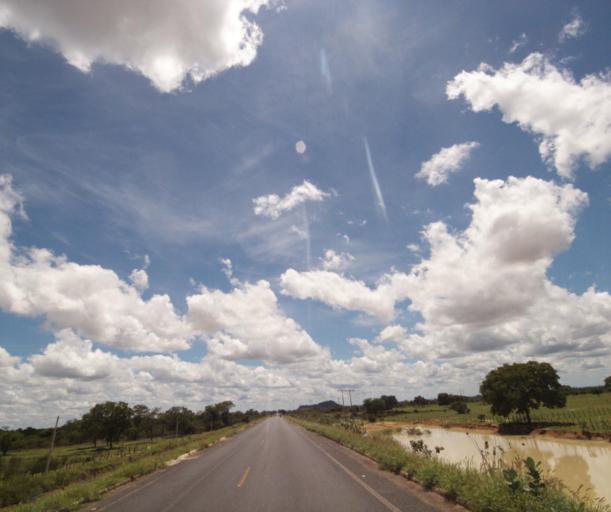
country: BR
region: Bahia
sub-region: Bom Jesus Da Lapa
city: Bom Jesus da Lapa
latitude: -13.2575
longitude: -43.4628
